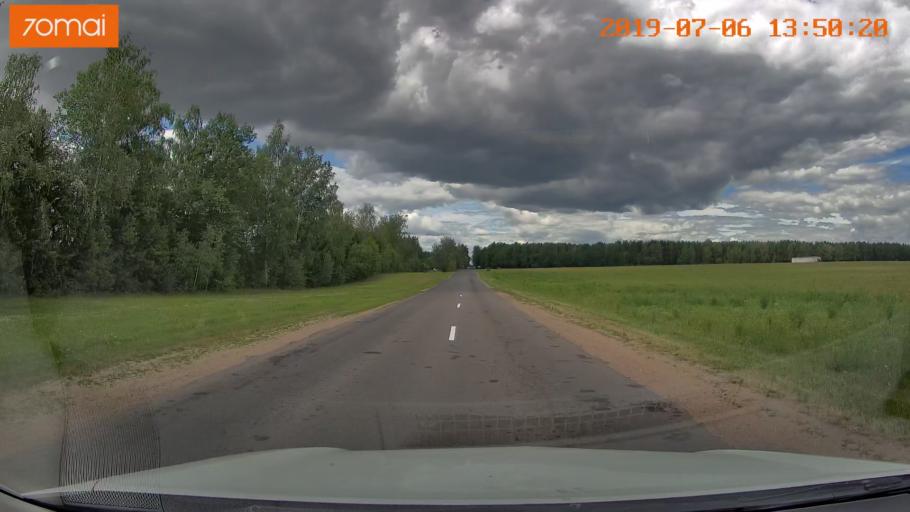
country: BY
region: Minsk
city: Ivyanyets
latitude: 53.6987
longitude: 26.8449
